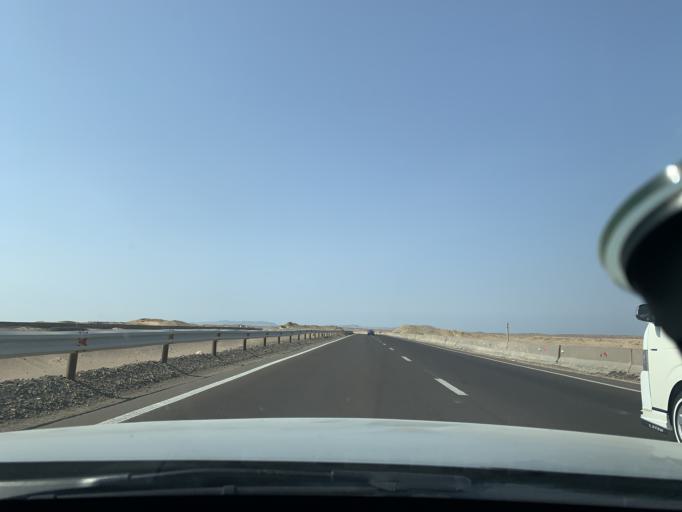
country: EG
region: Red Sea
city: El Gouna
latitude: 27.7280
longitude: 33.5072
